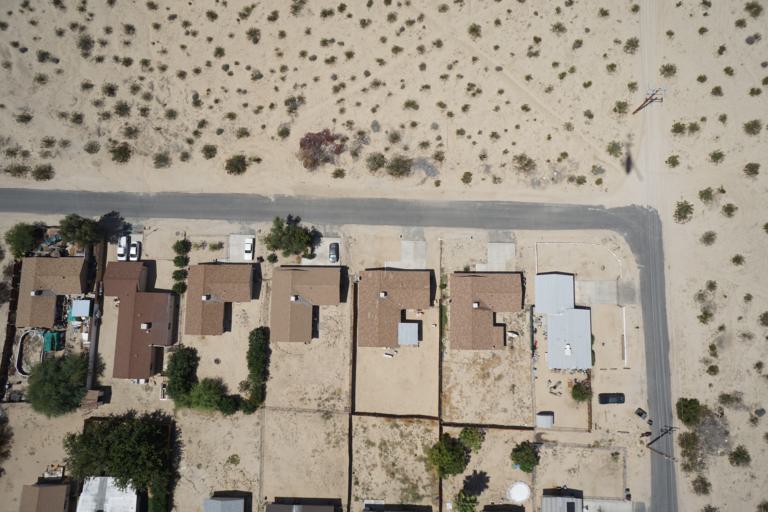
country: US
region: California
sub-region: San Bernardino County
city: Twentynine Palms
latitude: 34.1371
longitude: -116.0438
